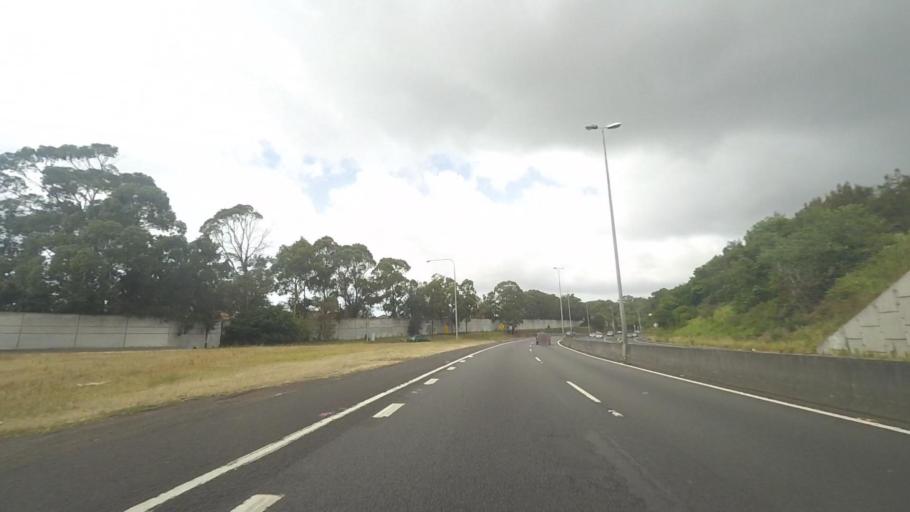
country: AU
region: New South Wales
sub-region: Wollongong
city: Gwynneville
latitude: -34.4134
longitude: 150.8826
